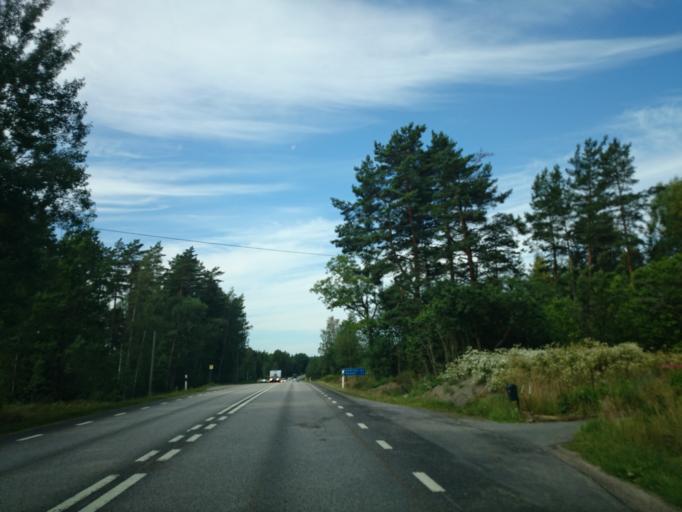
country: SE
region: Kalmar
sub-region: Vasterviks Kommun
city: Vaestervik
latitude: 57.7238
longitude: 16.4984
